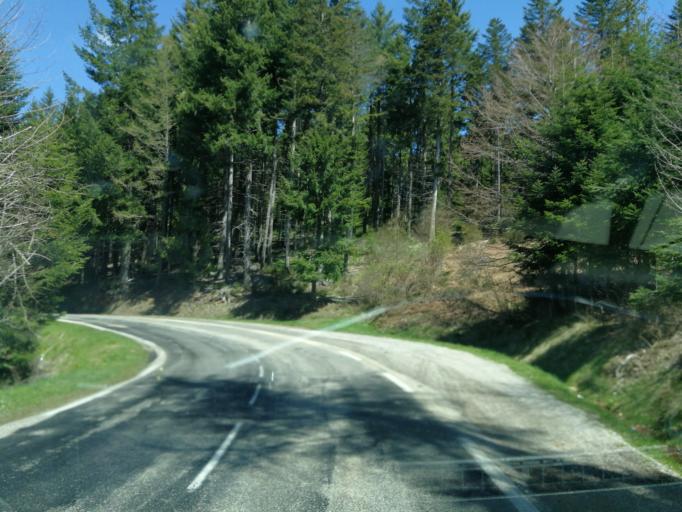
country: FR
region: Rhone-Alpes
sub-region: Departement de l'Ardeche
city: Saint-Agreve
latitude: 45.0232
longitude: 4.4070
